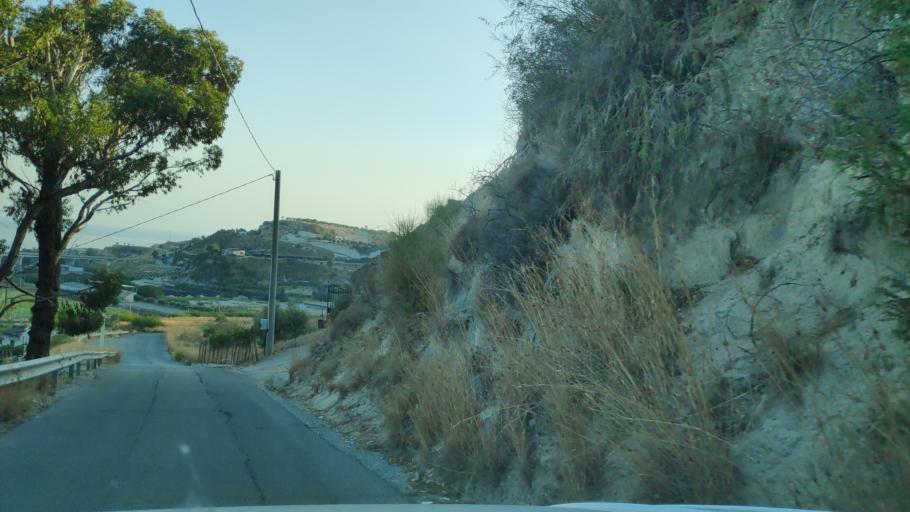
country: IT
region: Calabria
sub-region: Provincia di Reggio Calabria
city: Bova Marina
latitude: 37.9393
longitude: 15.9131
